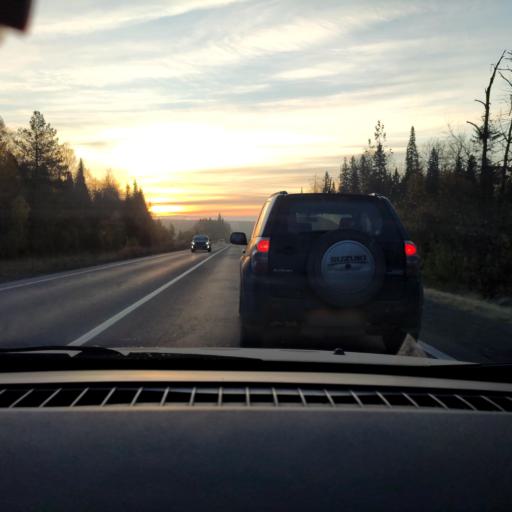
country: RU
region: Perm
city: Novyye Lyady
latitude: 58.0419
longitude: 56.4514
